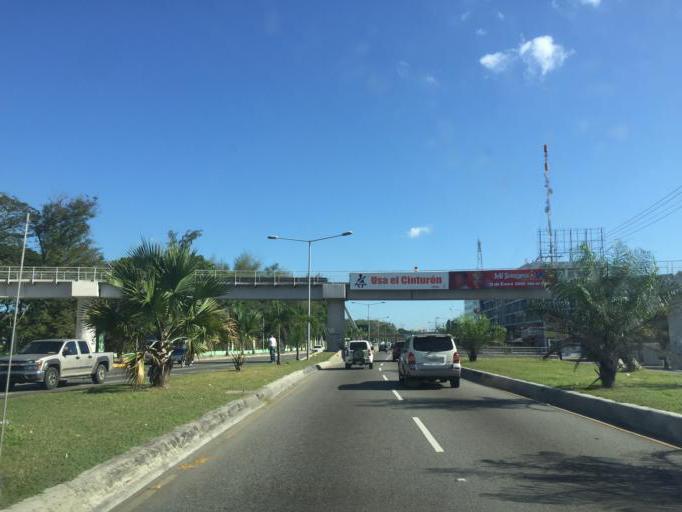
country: DO
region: Nacional
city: La Julia
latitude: 18.4730
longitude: -69.9188
